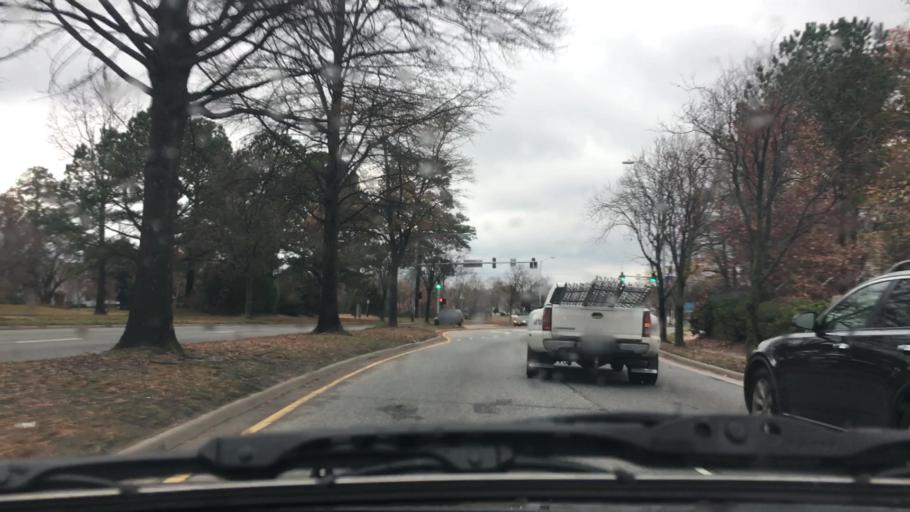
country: US
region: Virginia
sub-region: City of Norfolk
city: Norfolk
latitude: 36.8505
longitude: -76.2482
